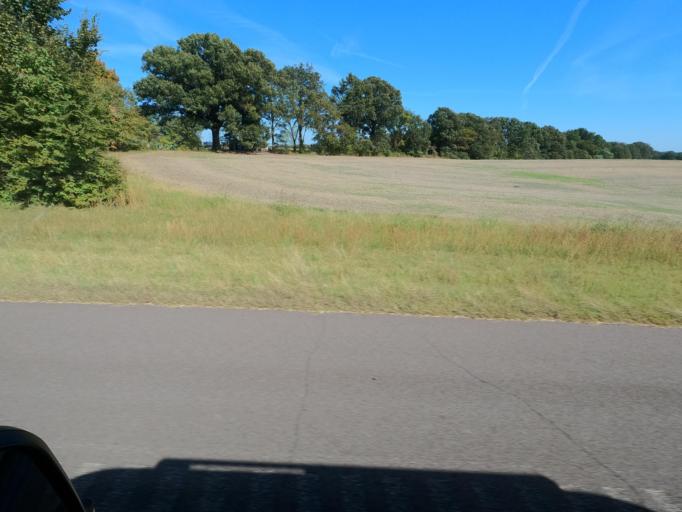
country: US
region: Tennessee
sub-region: Lauderdale County
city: Halls
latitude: 35.9380
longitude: -89.2943
